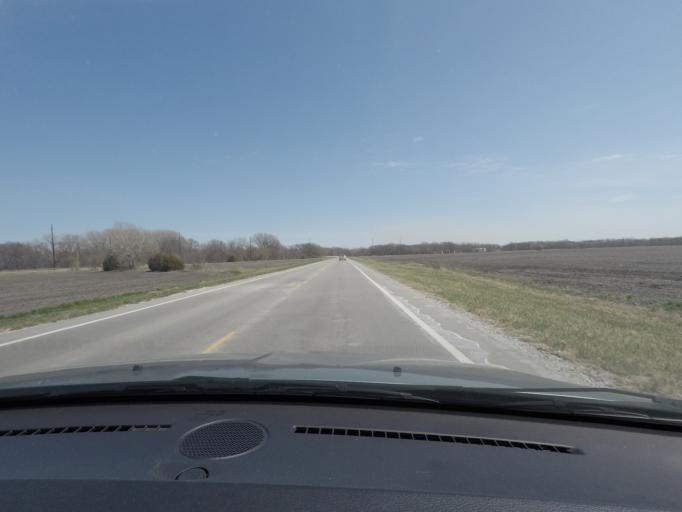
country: US
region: Kansas
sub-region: Lyon County
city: Emporia
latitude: 38.4320
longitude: -96.1765
